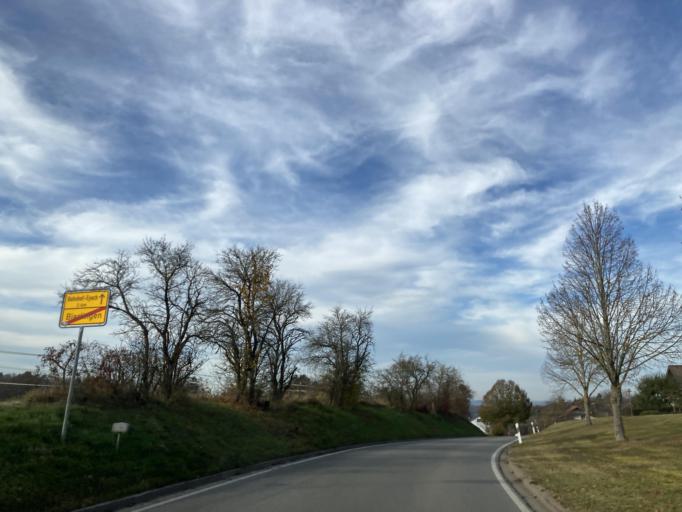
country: DE
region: Baden-Wuerttemberg
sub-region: Tuebingen Region
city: Haigerloch
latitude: 48.4351
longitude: 8.8102
